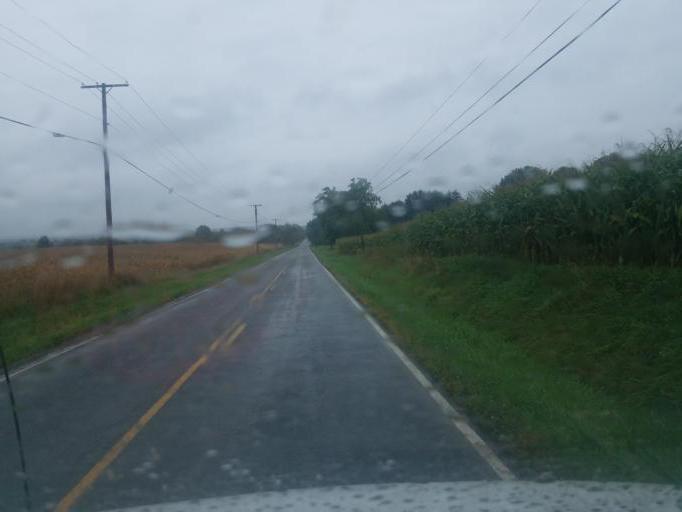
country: US
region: Ohio
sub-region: Medina County
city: Seville
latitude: 41.0100
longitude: -81.8365
